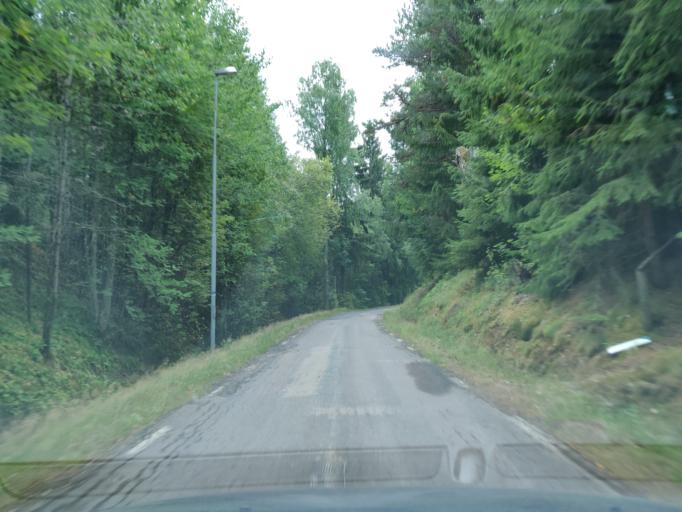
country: SE
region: Vaermland
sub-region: Munkfors Kommun
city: Munkfors
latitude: 59.9238
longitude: 13.5705
